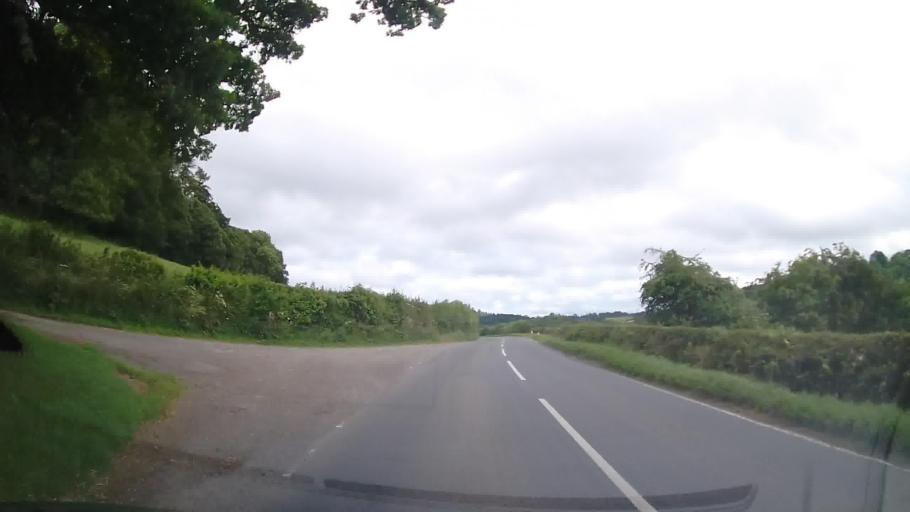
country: GB
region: Wales
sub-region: Sir Powys
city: Llanfechain
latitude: 52.8065
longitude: -3.1841
